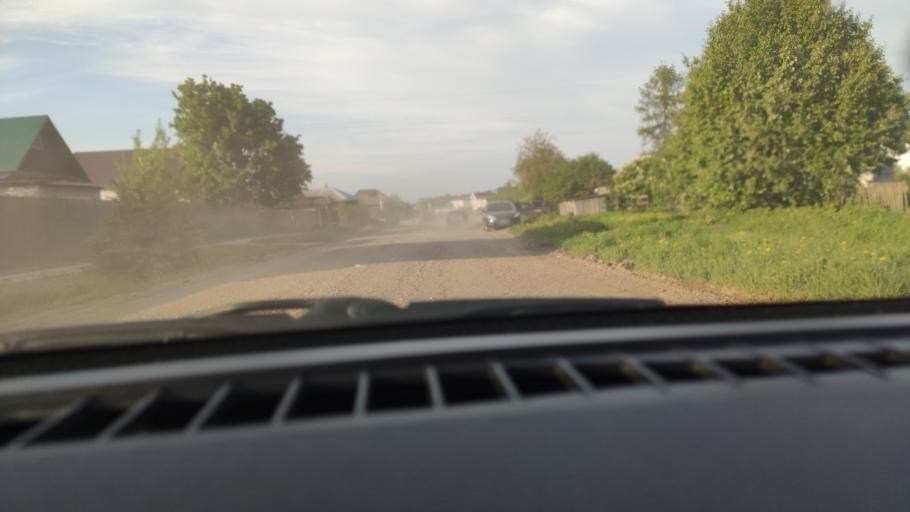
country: RU
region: Perm
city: Kultayevo
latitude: 57.9227
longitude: 56.0062
